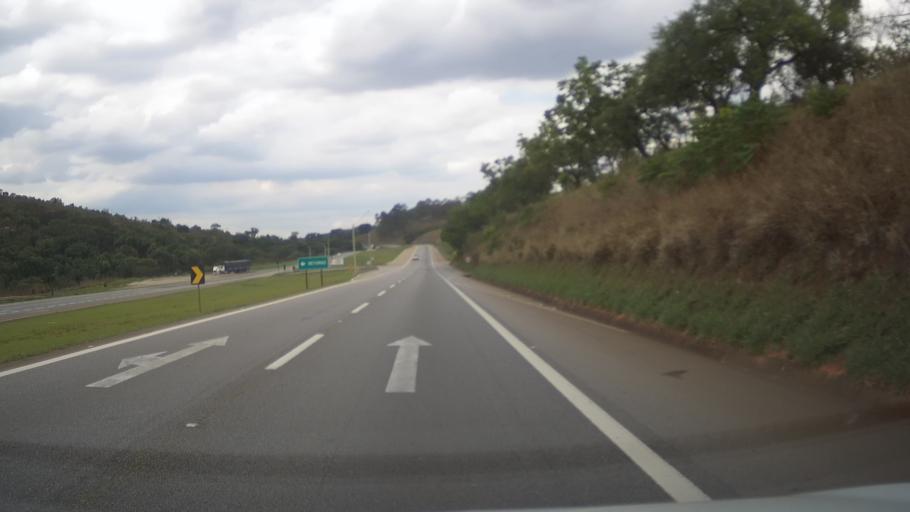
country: BR
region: Minas Gerais
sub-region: Tres Coracoes
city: Tres Coracoes
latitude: -21.5283
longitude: -45.2292
